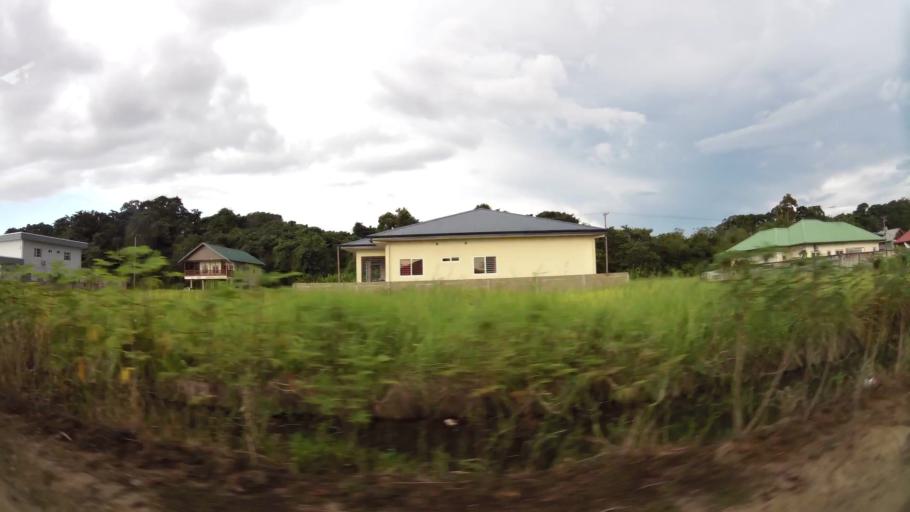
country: SR
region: Paramaribo
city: Paramaribo
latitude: 5.8633
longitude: -55.1799
